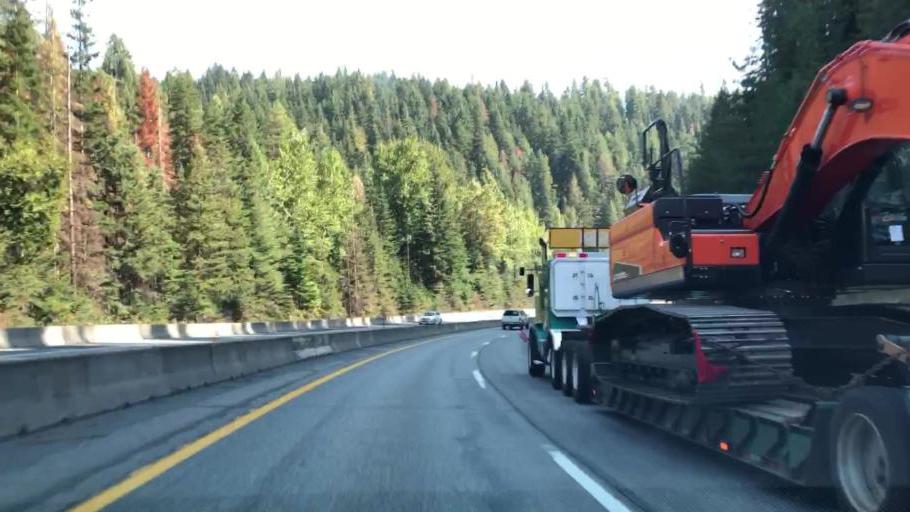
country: US
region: Idaho
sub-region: Shoshone County
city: Pinehurst
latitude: 47.5970
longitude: -116.4956
